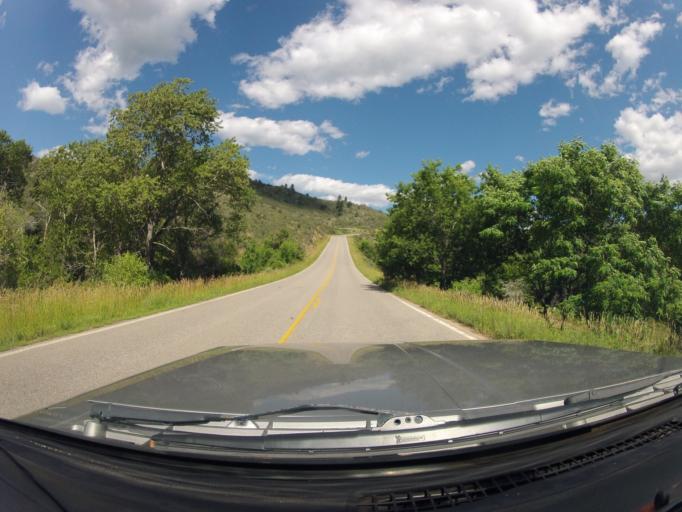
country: US
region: Colorado
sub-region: Larimer County
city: Laporte
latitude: 40.5469
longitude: -105.2848
